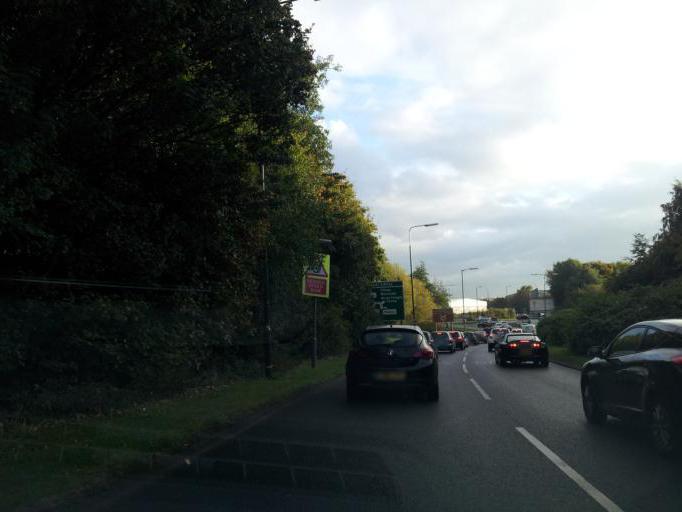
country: GB
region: England
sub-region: City and Borough of Salford
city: Eccles
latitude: 53.4680
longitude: -2.3283
